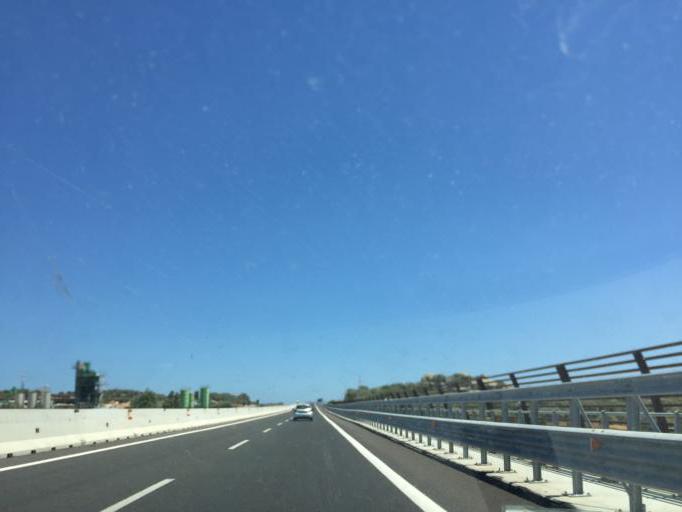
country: IT
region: Sardinia
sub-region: Provincia di Olbia-Tempio
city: Loiri Porto San Paolo
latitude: 40.8812
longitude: 9.4684
